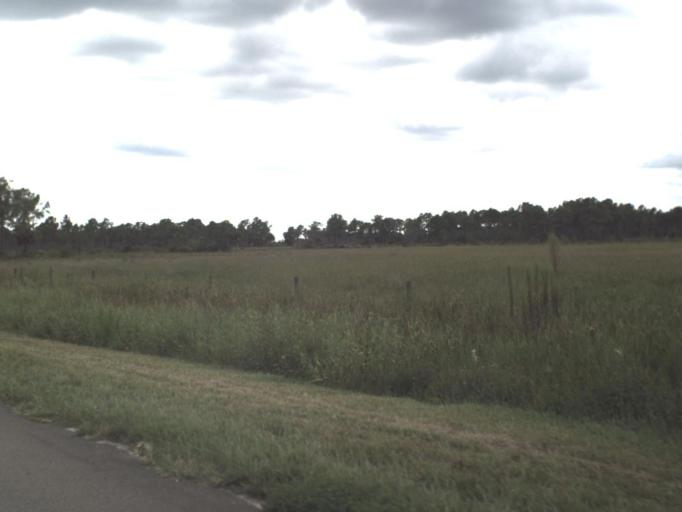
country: US
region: Florida
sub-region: Lee County
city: Olga
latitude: 26.8442
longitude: -81.7598
